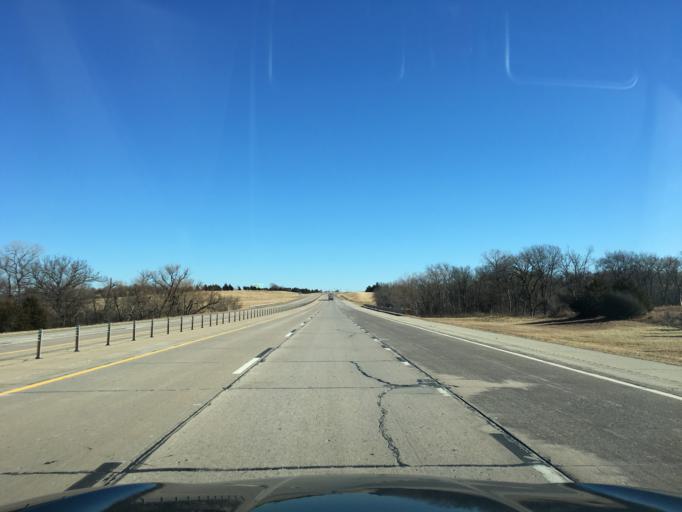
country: US
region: Oklahoma
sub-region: Pawnee County
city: Pawnee
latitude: 36.2399
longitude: -96.9416
